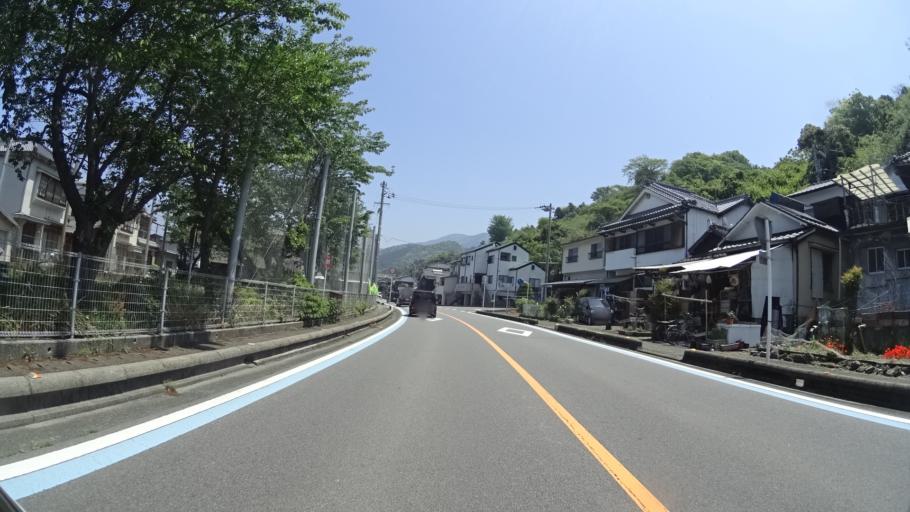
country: JP
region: Ehime
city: Ozu
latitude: 33.6503
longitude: 132.5746
